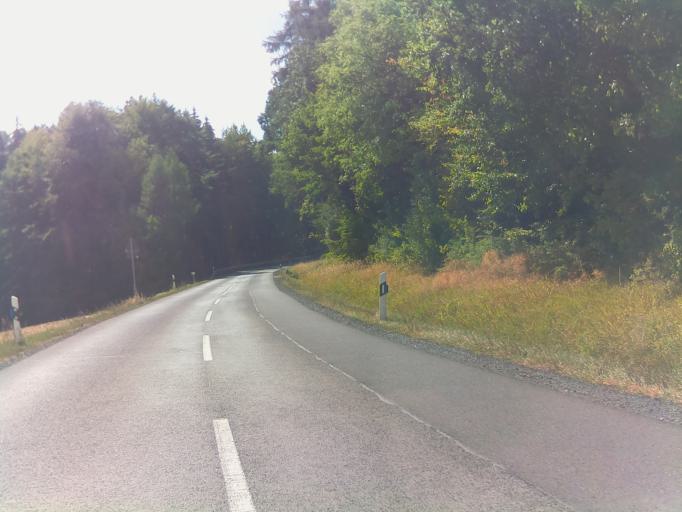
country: DE
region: Bavaria
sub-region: Regierungsbezirk Unterfranken
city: Sondheim vor der Rhoen
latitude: 50.4496
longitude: 10.1887
